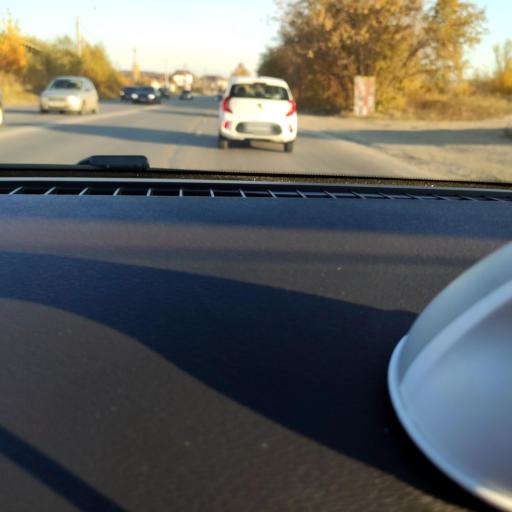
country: RU
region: Samara
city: Petra-Dubrava
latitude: 53.2710
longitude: 50.2753
